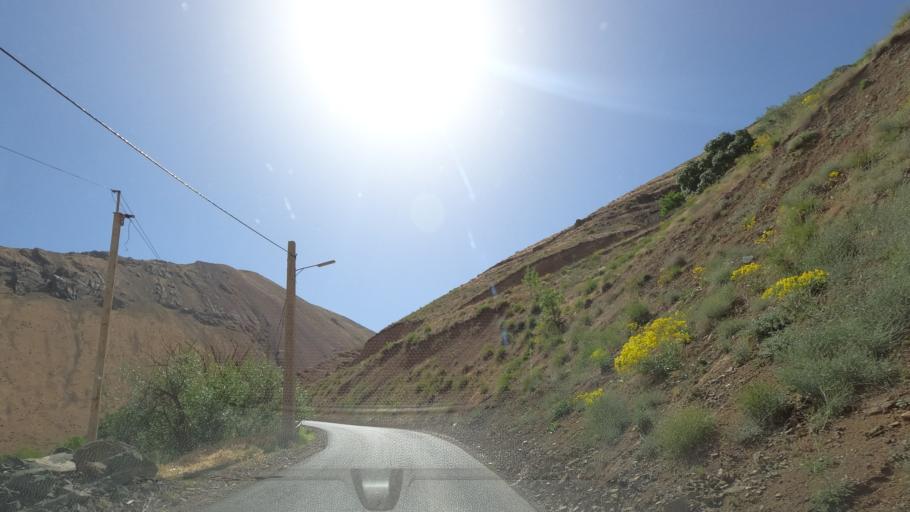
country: IR
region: Alborz
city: Karaj
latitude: 35.9405
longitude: 51.0859
